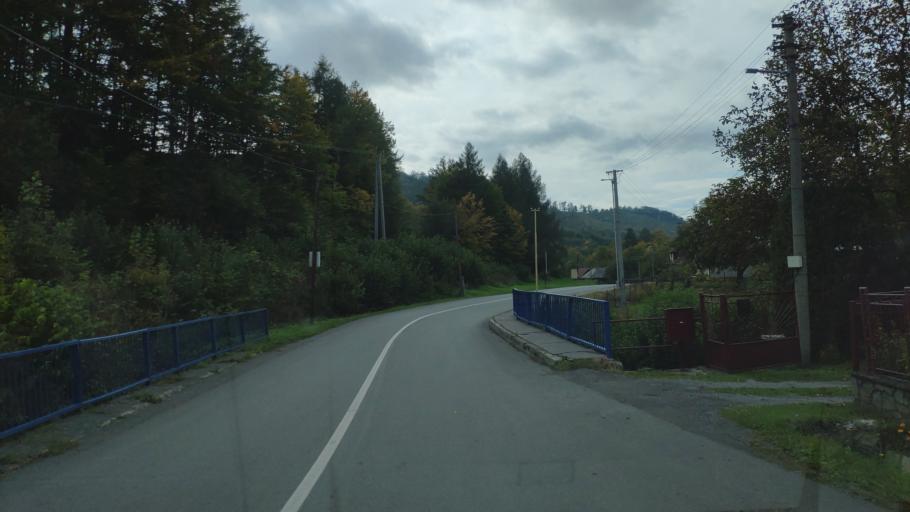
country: SK
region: Presovsky
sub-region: Okres Presov
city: Presov
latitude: 48.9513
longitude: 21.4148
